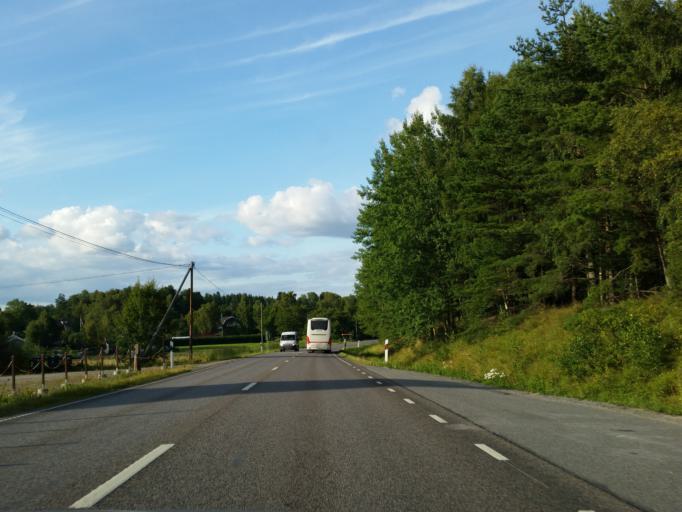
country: SE
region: Stockholm
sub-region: Sodertalje Kommun
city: Molnbo
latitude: 59.0744
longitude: 17.5381
